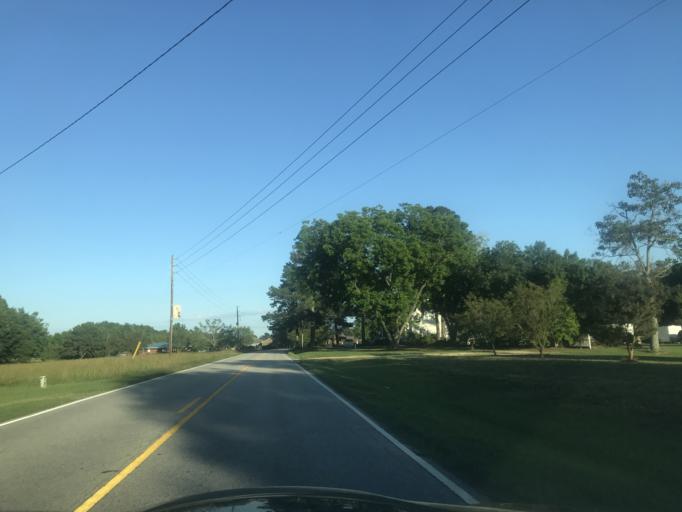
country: US
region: North Carolina
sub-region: Johnston County
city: Archer Lodge
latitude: 35.6999
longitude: -78.3804
